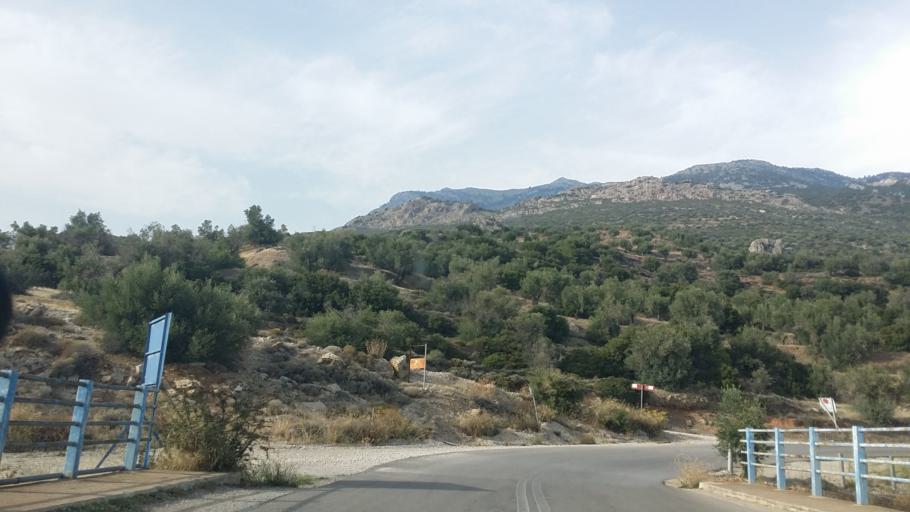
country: GR
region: Central Greece
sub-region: Nomos Voiotias
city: Korini
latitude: 38.2576
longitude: 22.8951
